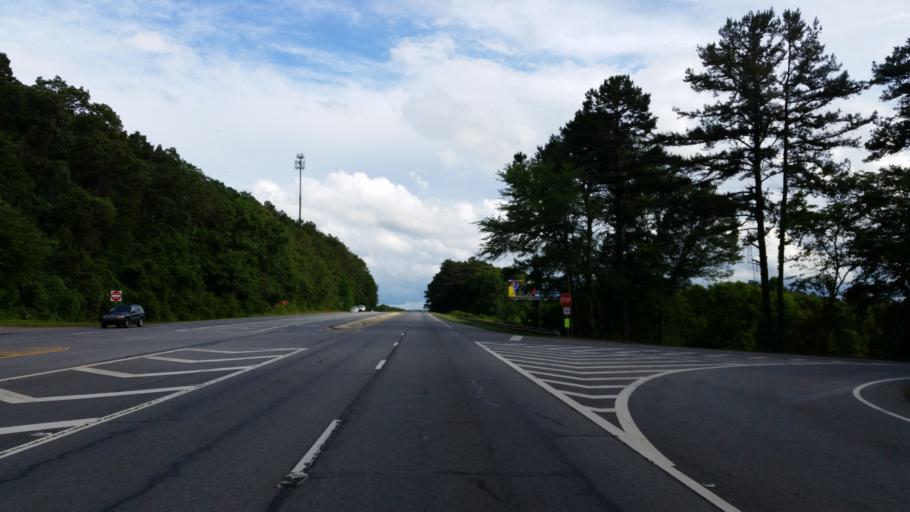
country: US
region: Georgia
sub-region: Bartow County
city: Emerson
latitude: 34.1272
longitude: -84.7517
